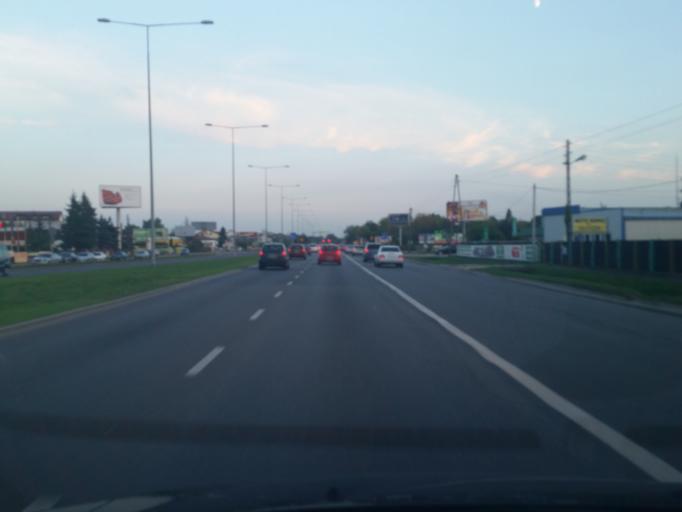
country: PL
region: Masovian Voivodeship
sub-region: Warszawa
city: Bialoleka
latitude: 52.3400
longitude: 20.9555
